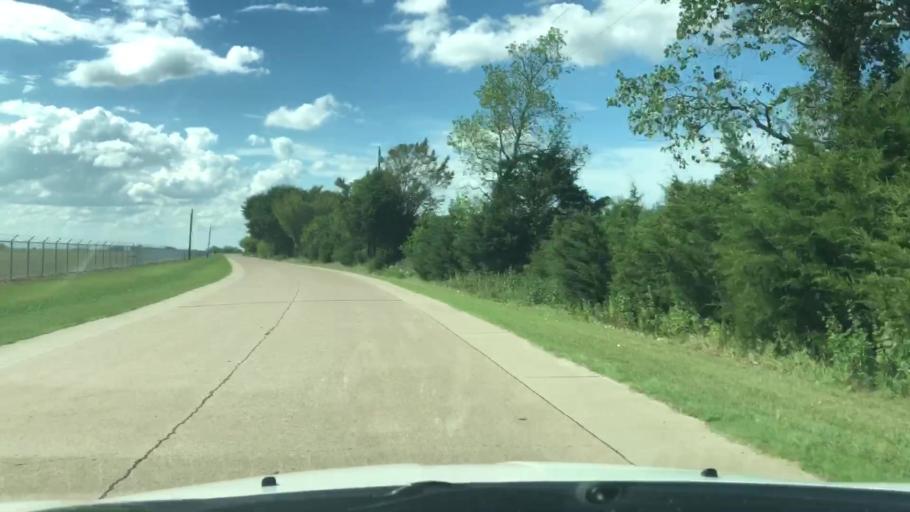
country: US
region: Texas
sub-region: Navarro County
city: Corsicana
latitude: 32.0322
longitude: -96.3971
